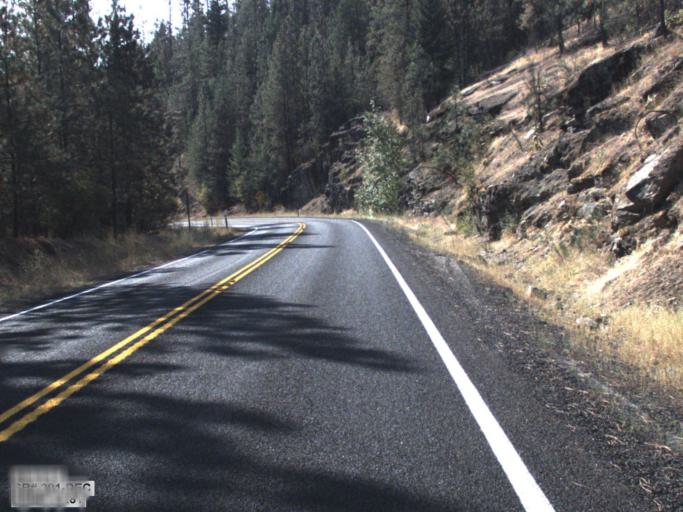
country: US
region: Washington
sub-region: Spokane County
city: Deer Park
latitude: 47.8783
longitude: -117.7048
